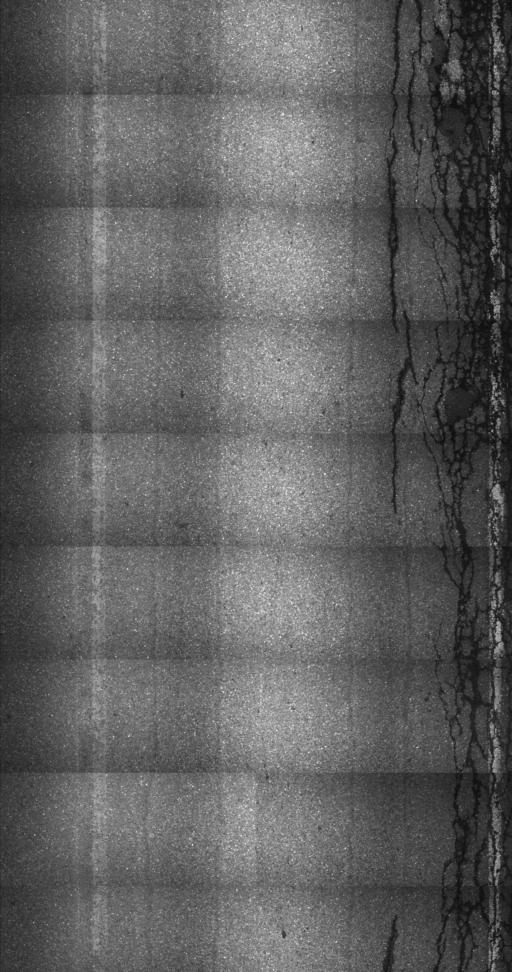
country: US
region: Vermont
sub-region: Addison County
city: Bristol
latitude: 44.1288
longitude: -73.0663
